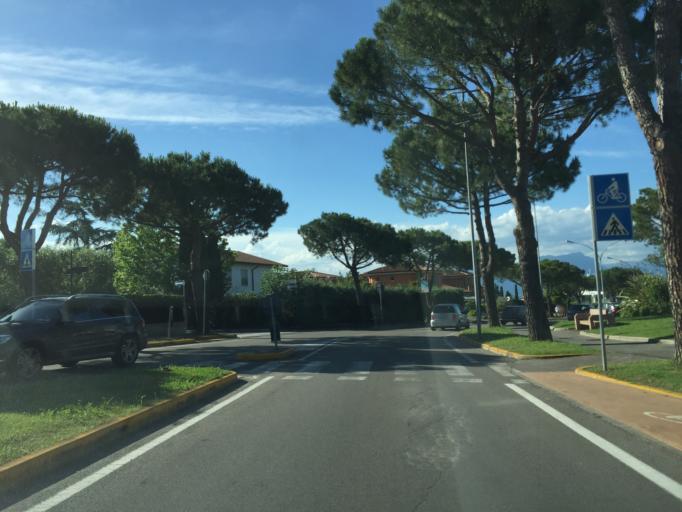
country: IT
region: Lombardy
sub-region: Provincia di Brescia
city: Sirmione
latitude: 45.4696
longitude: 10.6046
